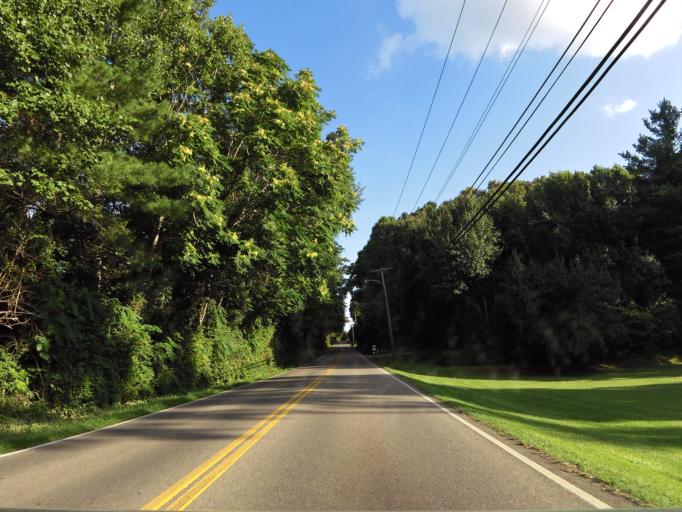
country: US
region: Tennessee
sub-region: Blount County
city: Maryville
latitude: 35.7310
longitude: -83.9650
